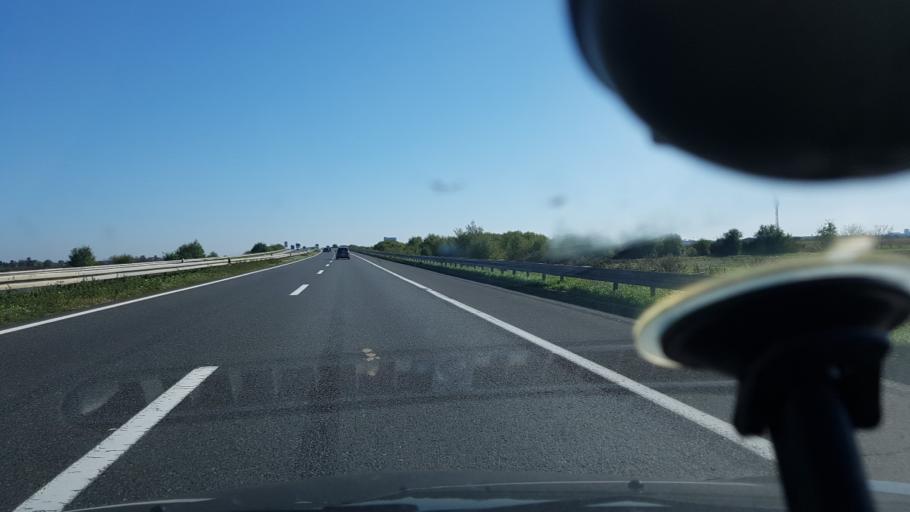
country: HR
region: Grad Zagreb
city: Odra
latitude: 45.7472
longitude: 16.0317
